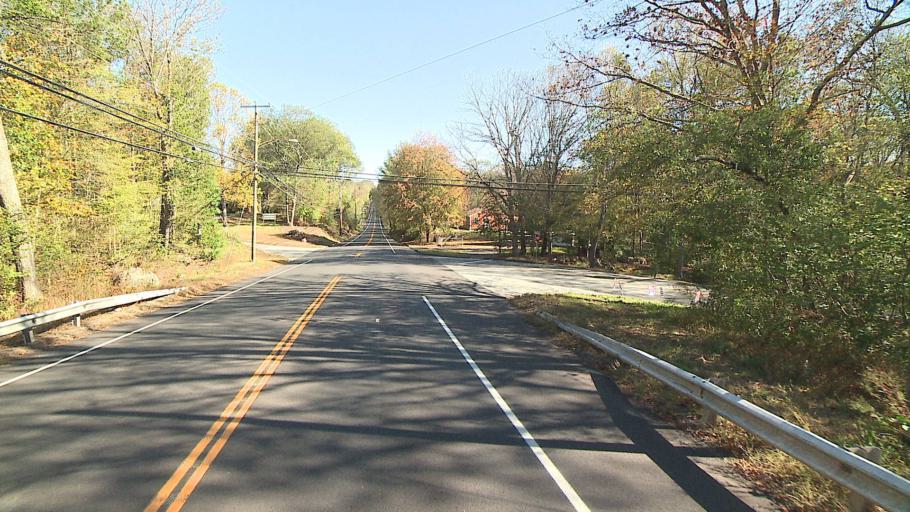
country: US
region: Connecticut
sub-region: Hartford County
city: Terramuggus
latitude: 41.6132
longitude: -72.4755
